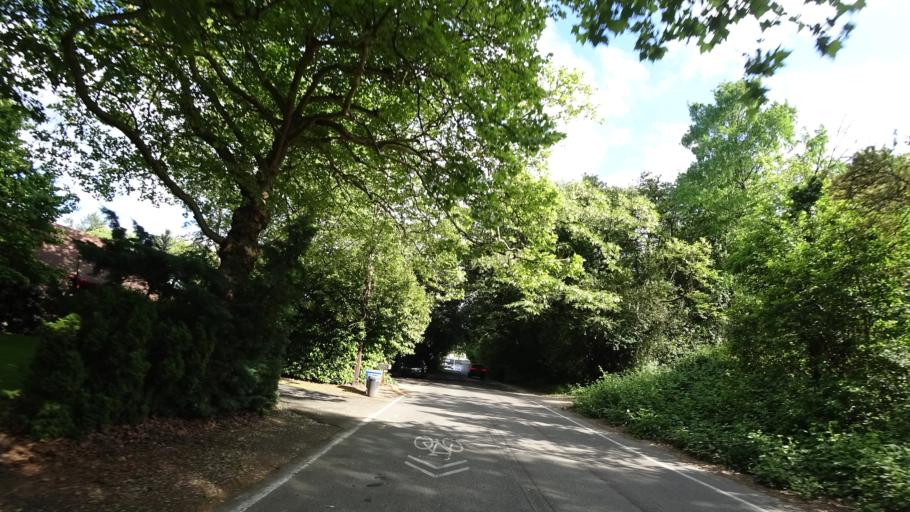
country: US
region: Oregon
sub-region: Washington County
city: Garden Home-Whitford
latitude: 45.4684
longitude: -122.7240
